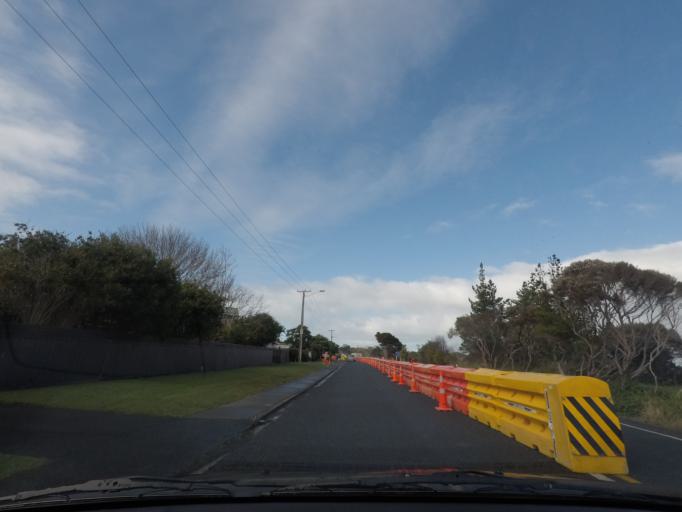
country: NZ
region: Auckland
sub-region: Auckland
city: Warkworth
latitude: -36.4330
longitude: 174.7385
